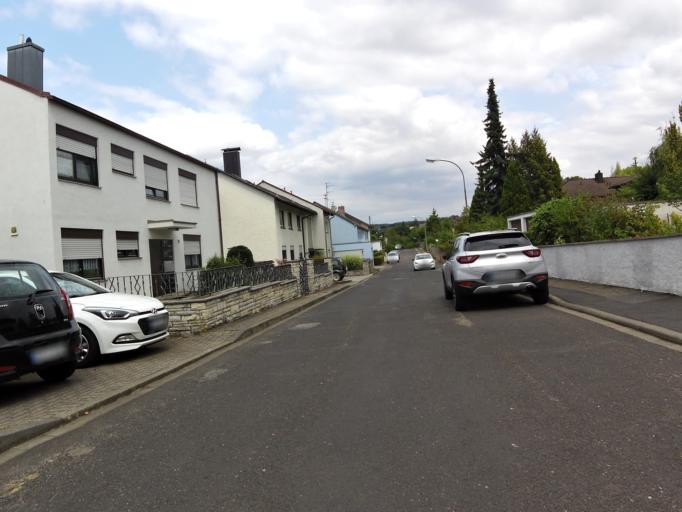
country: DE
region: Bavaria
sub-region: Regierungsbezirk Unterfranken
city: Veitshochheim
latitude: 49.8265
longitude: 9.8816
